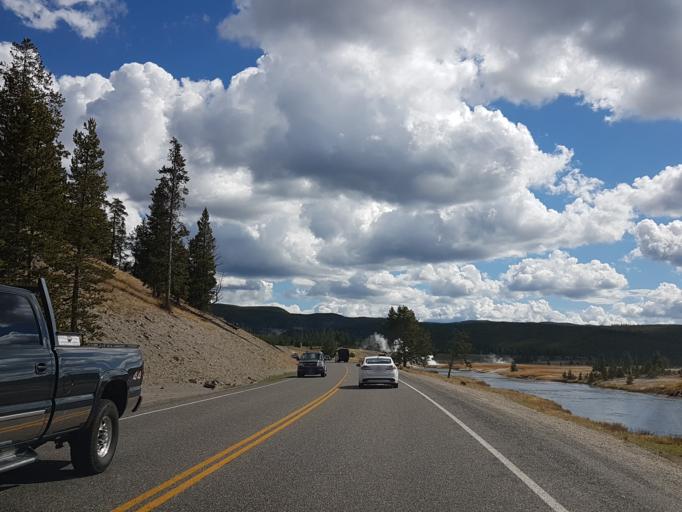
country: US
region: Montana
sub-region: Gallatin County
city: West Yellowstone
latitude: 44.5257
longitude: -110.8337
